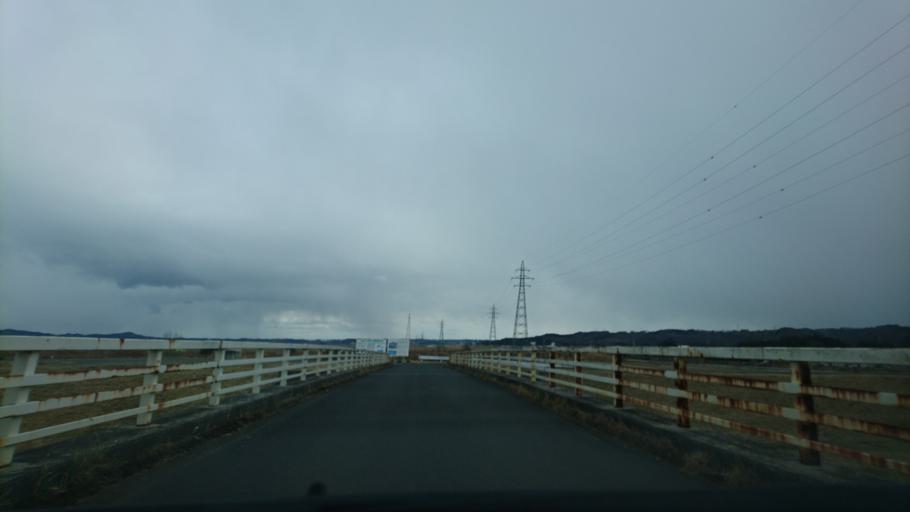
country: JP
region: Iwate
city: Ichinoseki
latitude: 38.9861
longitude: 141.1217
